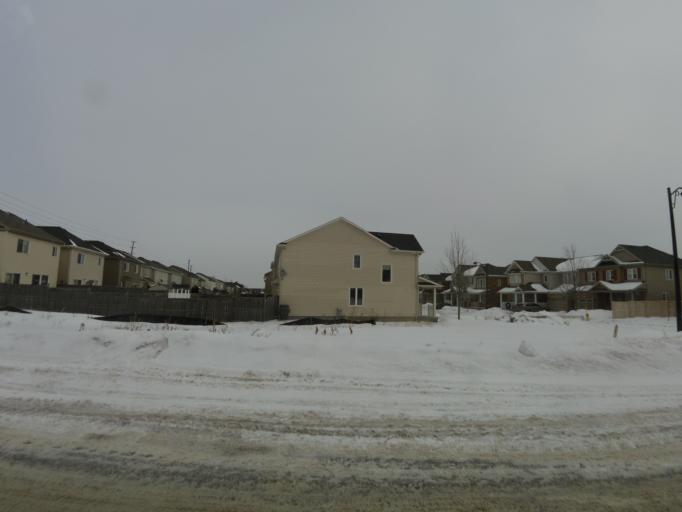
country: CA
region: Ontario
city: Bells Corners
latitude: 45.2864
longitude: -75.9235
